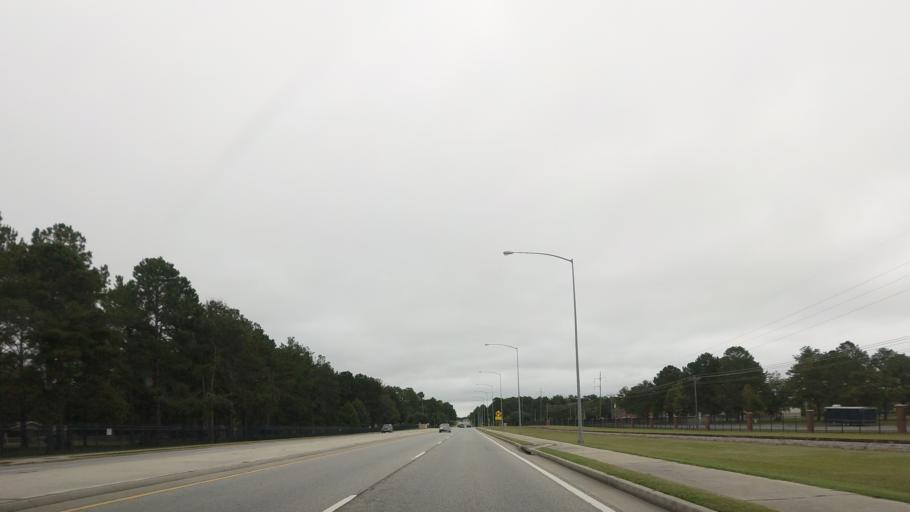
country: US
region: Georgia
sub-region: Berrien County
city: Ray City
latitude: 30.9761
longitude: -83.2114
